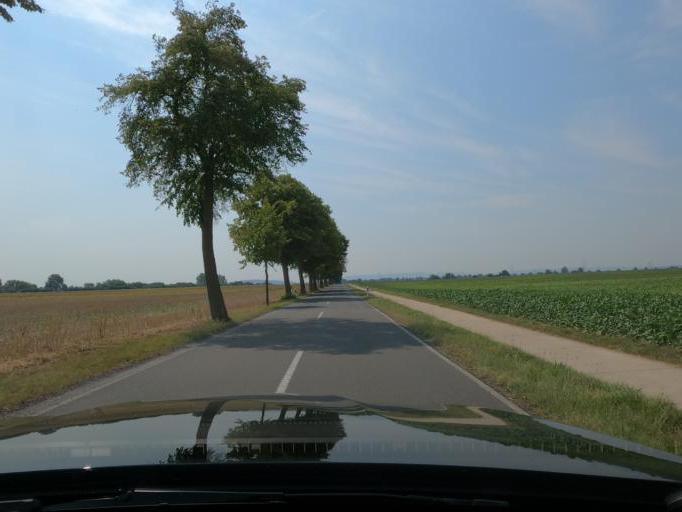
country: DE
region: Lower Saxony
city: Sarstedt
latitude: 52.2287
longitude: 9.8122
